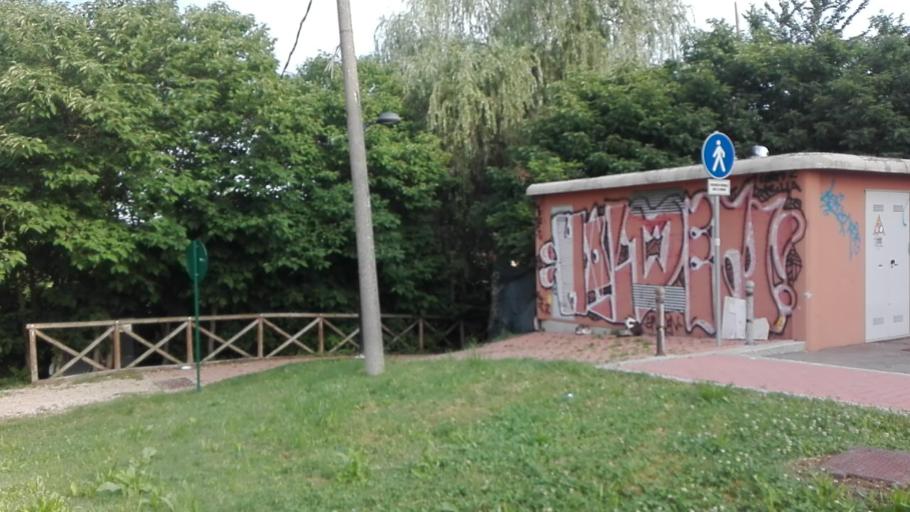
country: IT
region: Emilia-Romagna
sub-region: Provincia di Bologna
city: Trebbo
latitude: 44.5318
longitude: 11.3427
